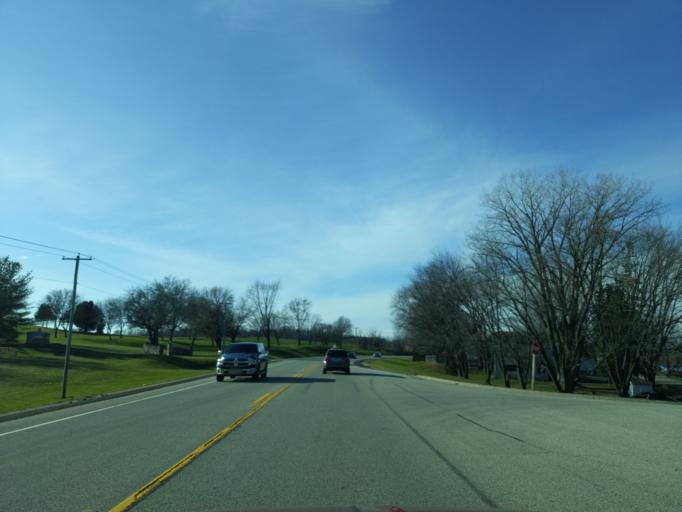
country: US
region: Wisconsin
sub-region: Rock County
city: Edgerton
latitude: 42.8270
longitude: -89.0150
